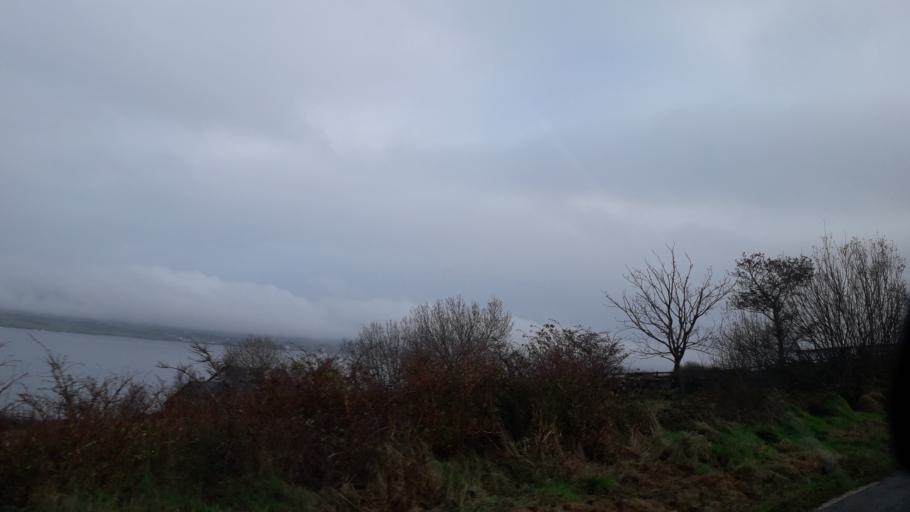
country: IE
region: Ulster
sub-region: County Donegal
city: Buncrana
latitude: 55.1560
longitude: -7.5603
